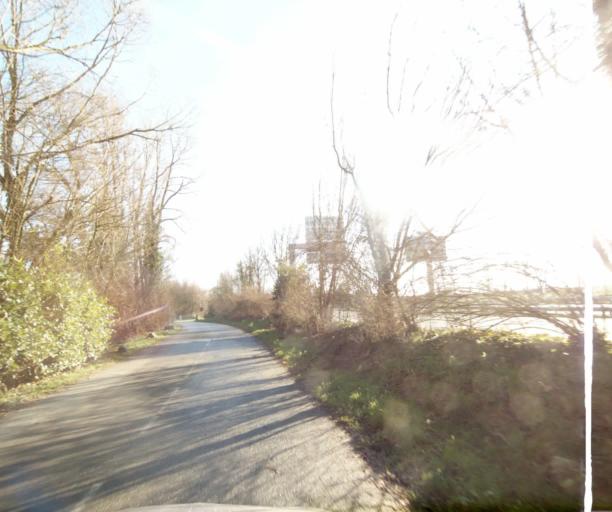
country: FR
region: Nord-Pas-de-Calais
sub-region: Departement du Nord
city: Curgies
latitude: 50.3245
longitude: 3.5982
